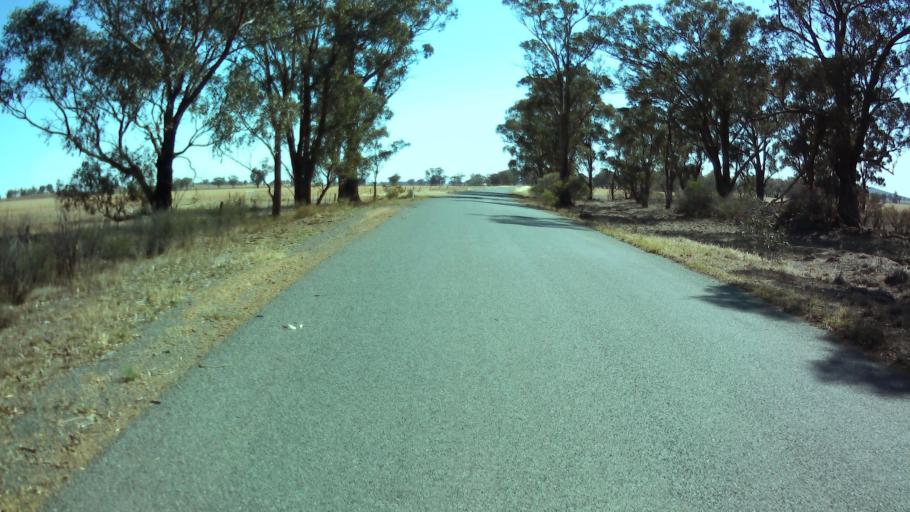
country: AU
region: New South Wales
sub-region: Weddin
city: Grenfell
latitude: -33.7370
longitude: 147.8838
